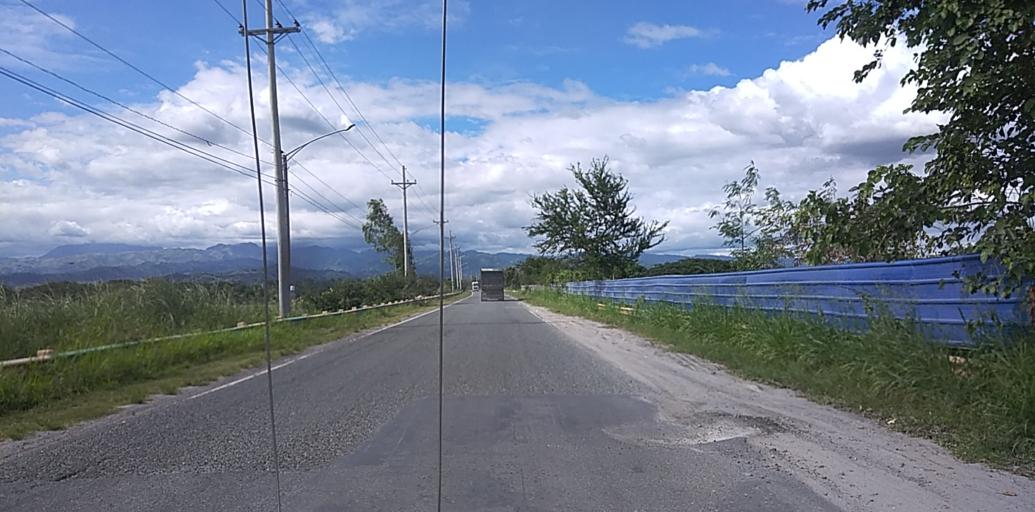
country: PH
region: Central Luzon
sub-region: Province of Pampanga
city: Porac
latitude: 15.0831
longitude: 120.5471
